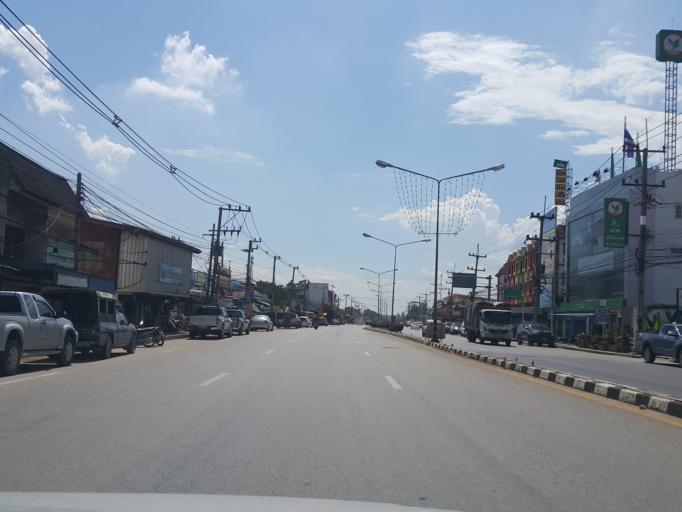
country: TH
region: Chiang Mai
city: Mae Taeng
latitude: 19.0940
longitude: 98.9365
